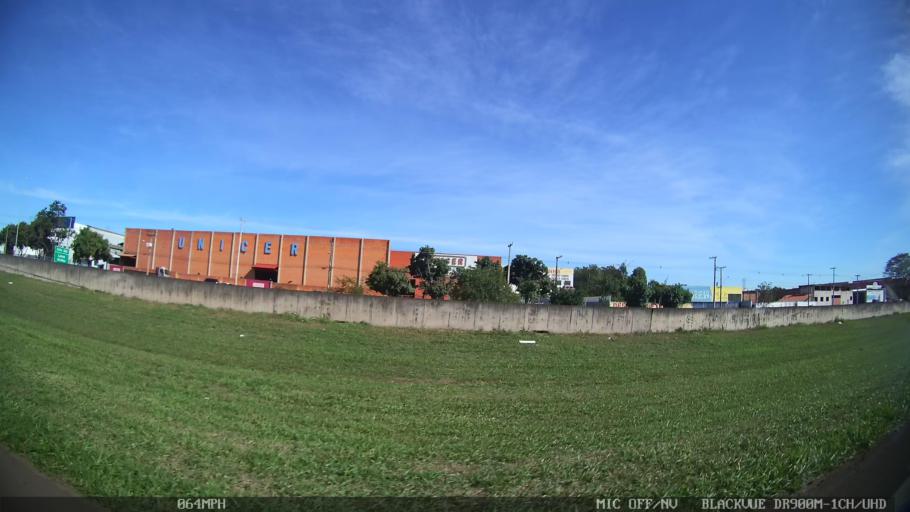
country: BR
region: Sao Paulo
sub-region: Leme
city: Leme
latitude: -22.1785
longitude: -47.3988
